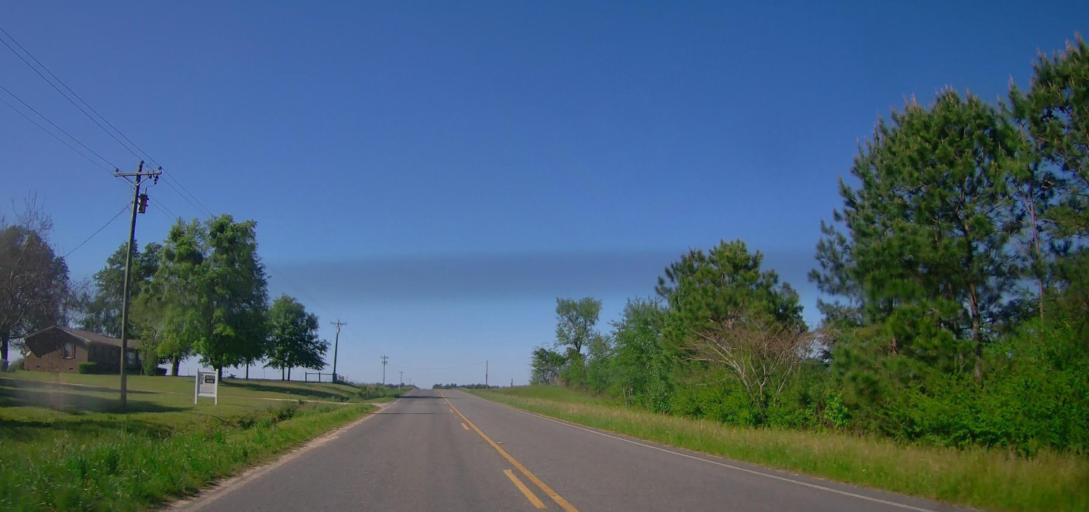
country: US
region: Georgia
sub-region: Wilcox County
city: Rochelle
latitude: 32.0681
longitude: -83.5035
